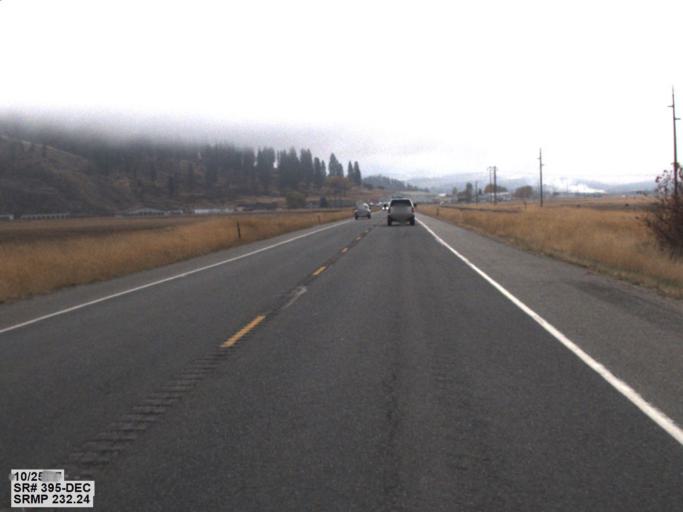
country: US
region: Washington
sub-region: Stevens County
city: Colville
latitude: 48.5723
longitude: -117.9442
